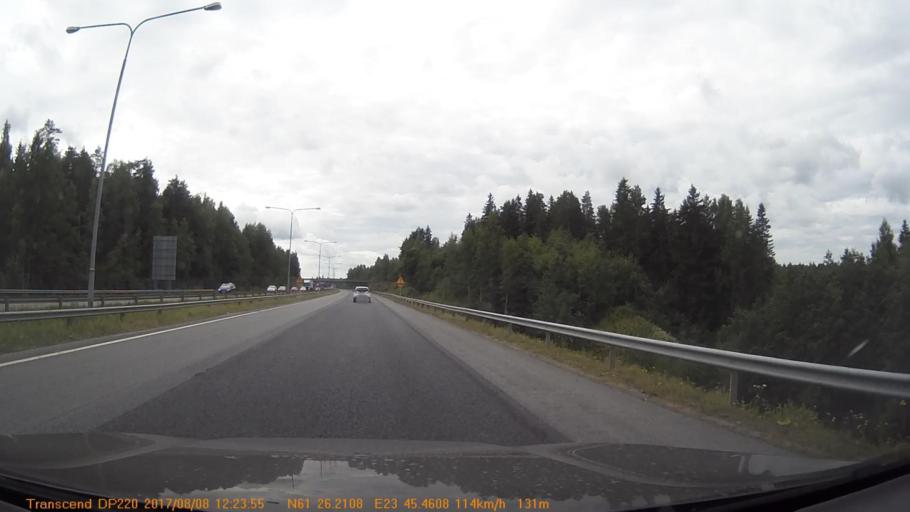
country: FI
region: Pirkanmaa
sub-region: Tampere
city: Tampere
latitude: 61.4364
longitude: 23.7574
